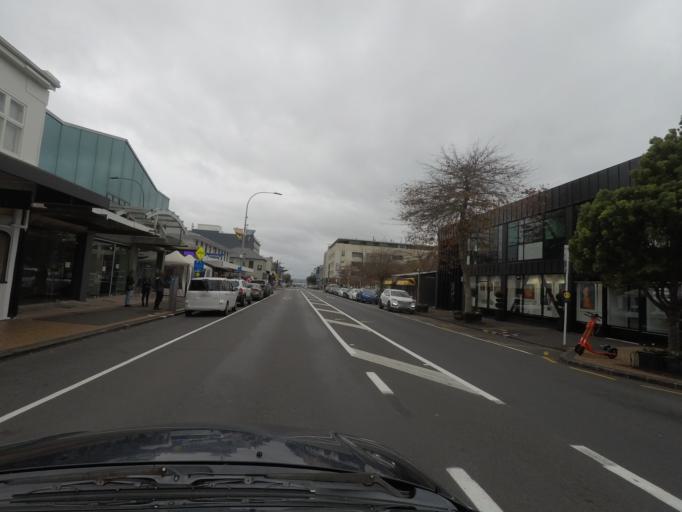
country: NZ
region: Auckland
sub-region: Auckland
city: Auckland
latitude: -36.8550
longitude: 174.7802
